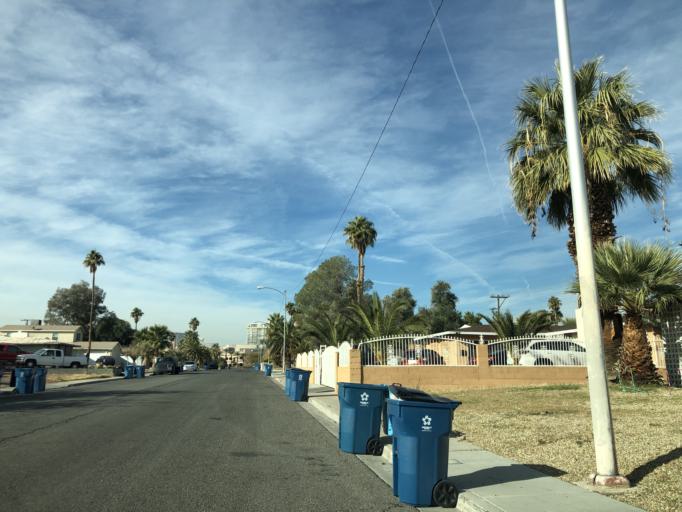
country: US
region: Nevada
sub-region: Clark County
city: Winchester
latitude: 36.1331
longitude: -115.1286
